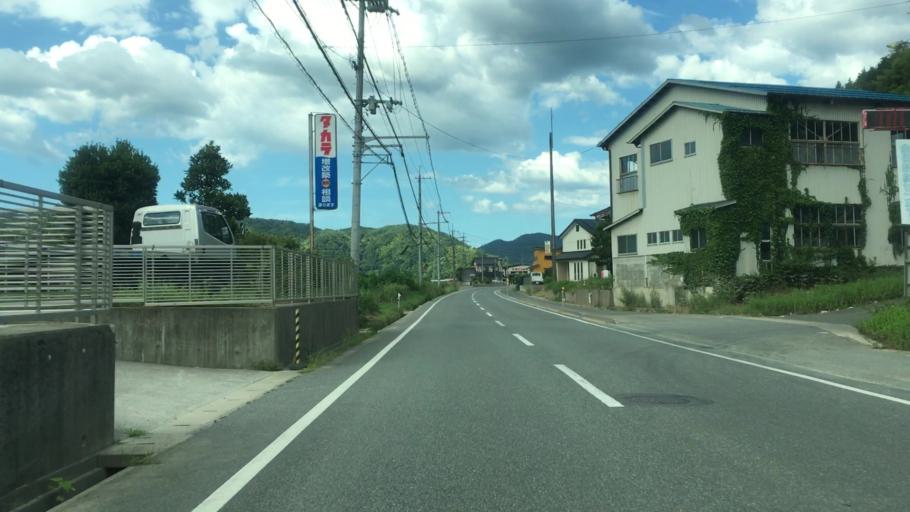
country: JP
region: Hyogo
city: Toyooka
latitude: 35.5539
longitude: 134.7934
